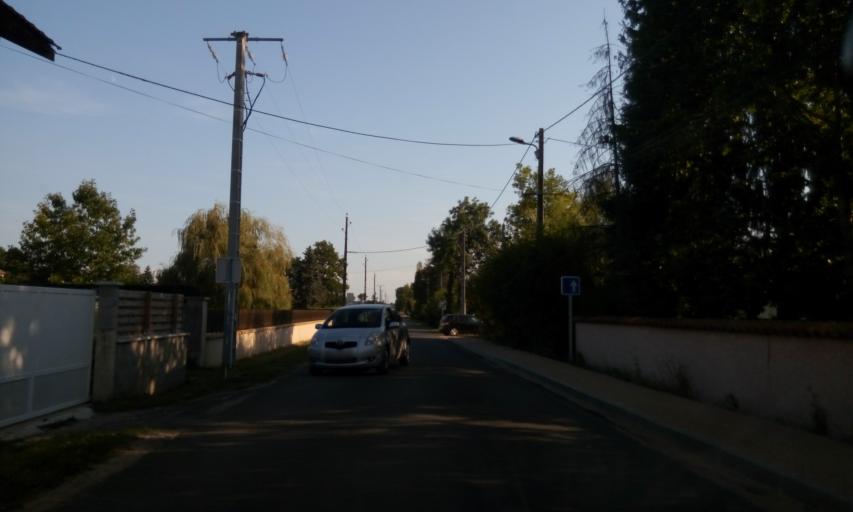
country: FR
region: Rhone-Alpes
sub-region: Departement de l'Ain
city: Villars-les-Dombes
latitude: 46.0199
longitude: 5.0900
